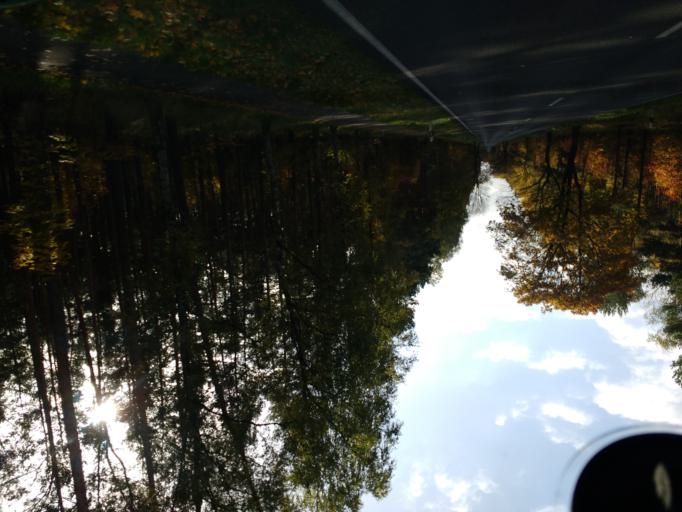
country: DE
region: Brandenburg
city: Grunheide
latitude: 52.3810
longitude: 13.8314
